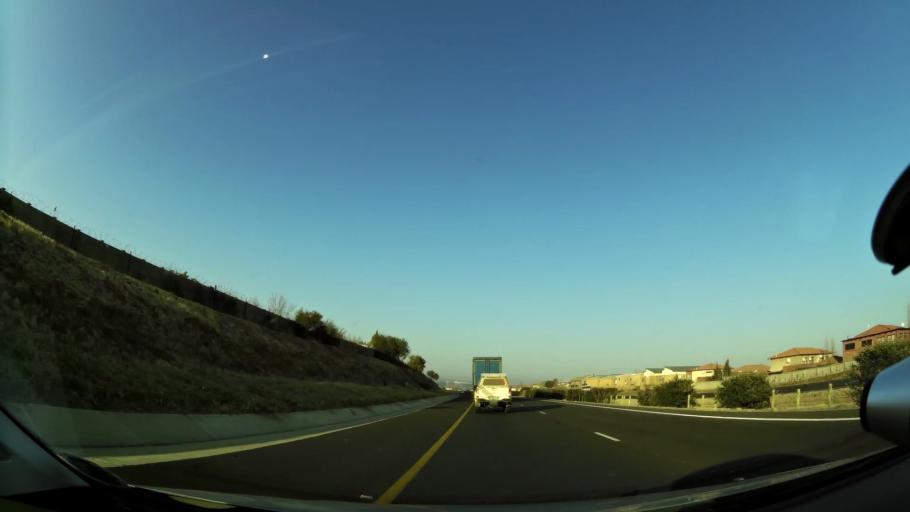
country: ZA
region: Orange Free State
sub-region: Mangaung Metropolitan Municipality
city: Bloemfontein
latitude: -29.0972
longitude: 26.1666
